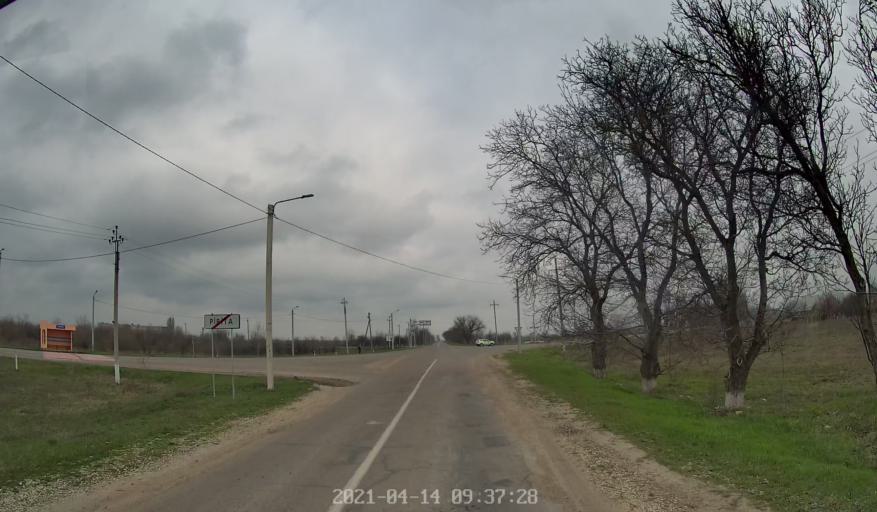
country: MD
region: Chisinau
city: Vadul lui Voda
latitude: 47.1186
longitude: 29.1111
